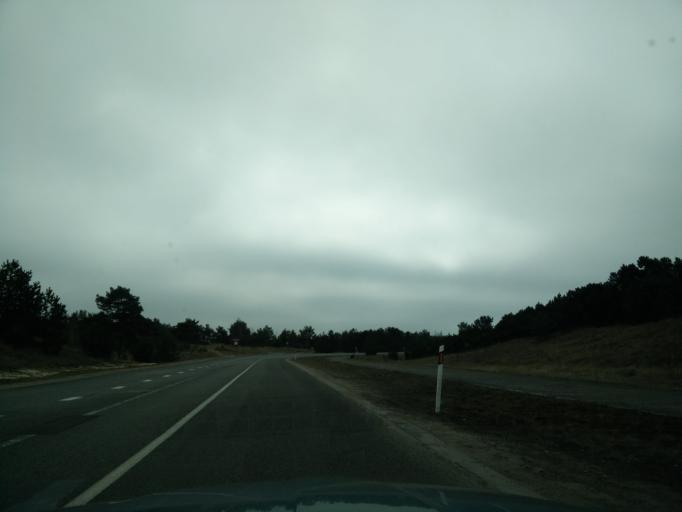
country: LT
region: Klaipedos apskritis
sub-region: Klaipeda
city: Klaipeda
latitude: 55.6837
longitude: 21.1295
